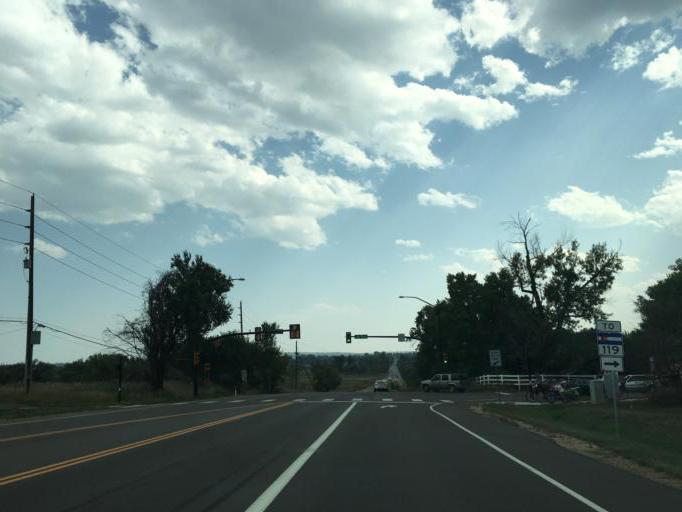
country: US
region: Colorado
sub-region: Boulder County
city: Gunbarrel
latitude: 40.0536
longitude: -105.1783
